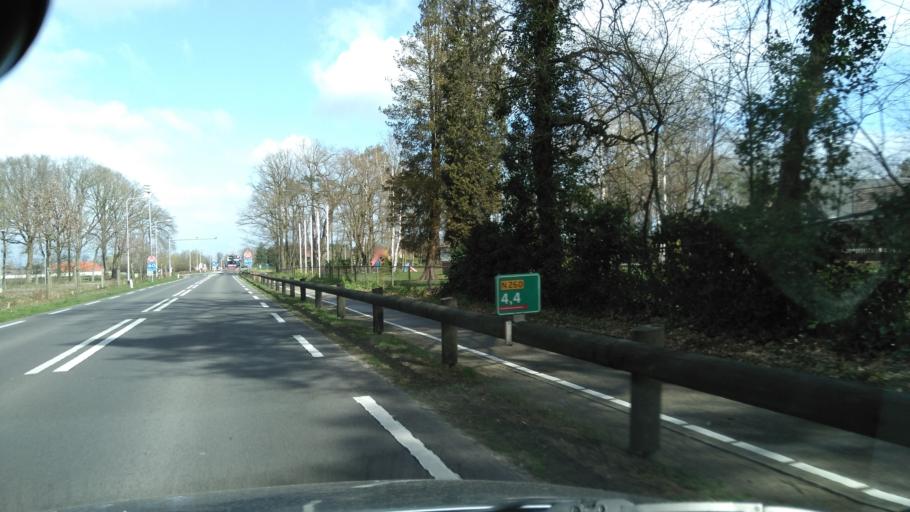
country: NL
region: North Brabant
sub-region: Gemeente Baarle-Nassau
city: Baarle-Nassau
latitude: 51.4235
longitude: 4.9337
